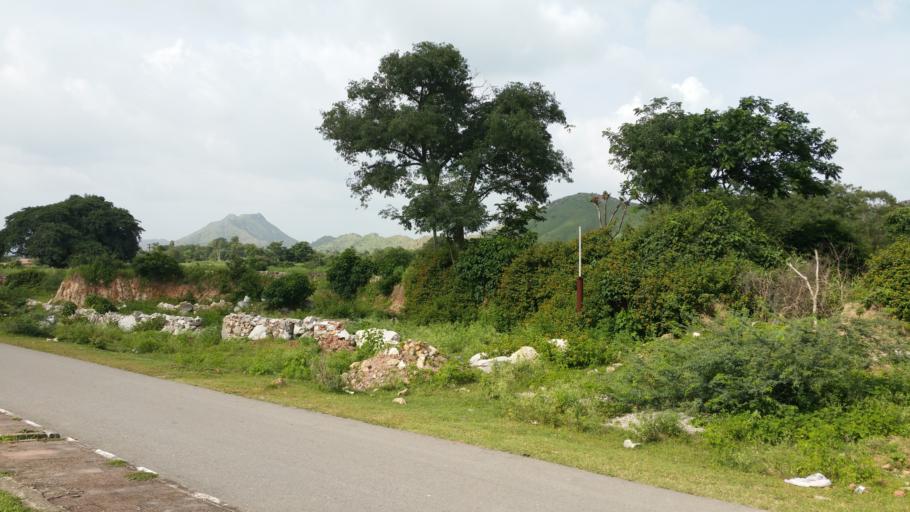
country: IN
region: Rajasthan
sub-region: Udaipur
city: Udaipur
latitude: 24.7578
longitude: 73.5384
